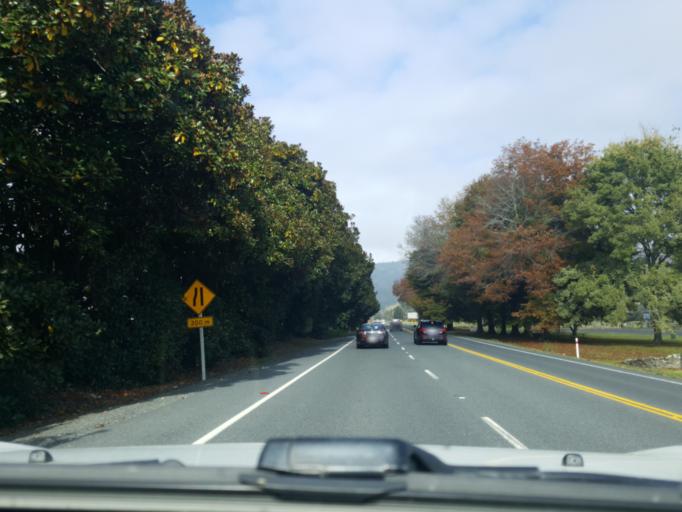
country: NZ
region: Waikato
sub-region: Waikato District
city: Ngaruawahia
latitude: -37.5840
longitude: 175.1595
